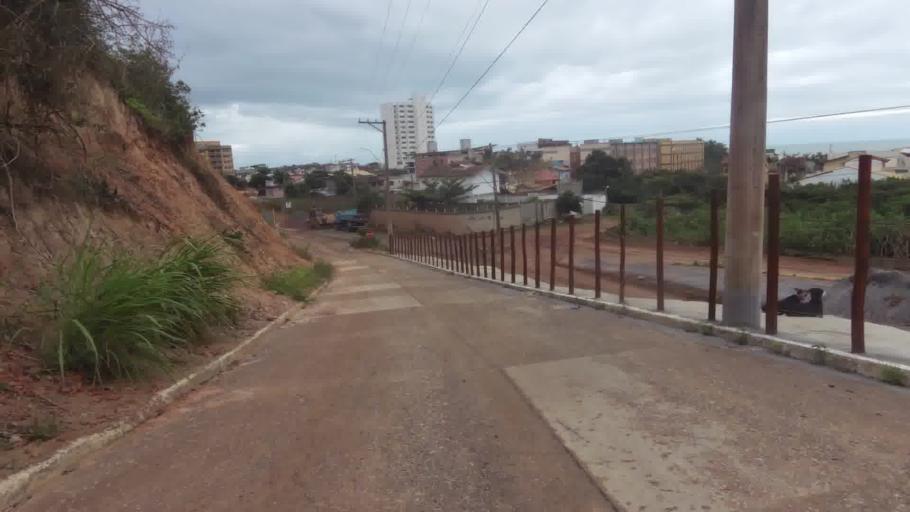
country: BR
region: Espirito Santo
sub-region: Marataizes
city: Marataizes
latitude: -21.0571
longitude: -40.8357
